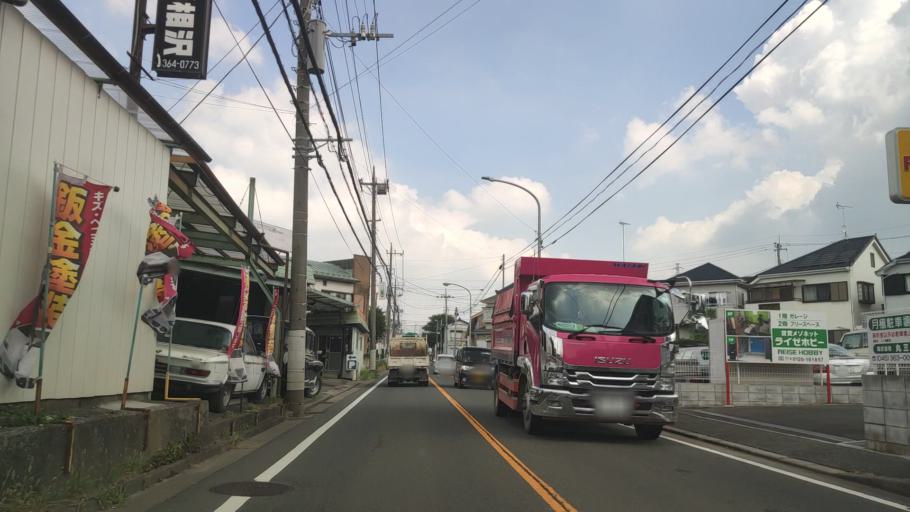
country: JP
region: Kanagawa
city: Minami-rinkan
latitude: 35.4488
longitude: 139.5038
